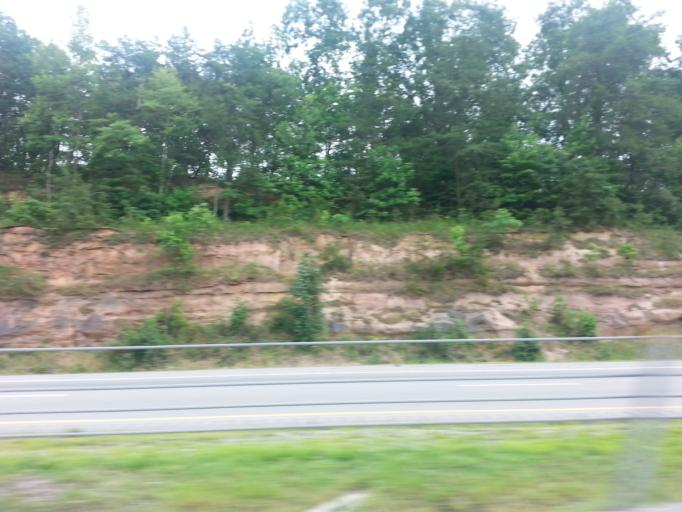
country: US
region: Tennessee
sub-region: Putnam County
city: Monterey
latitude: 36.1359
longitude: -85.3129
